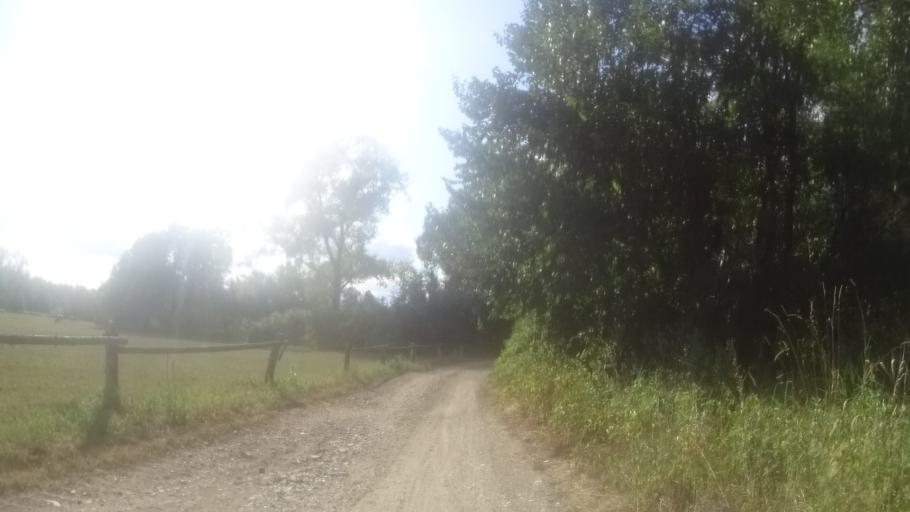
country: CZ
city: Albrechtice nad Orlici
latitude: 50.1613
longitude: 16.0415
